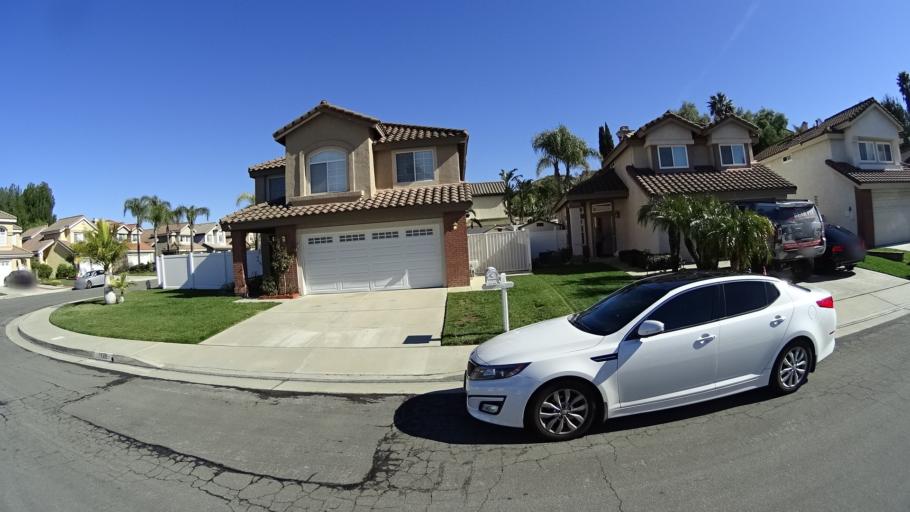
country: US
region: California
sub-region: Orange County
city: Villa Park
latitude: 33.8494
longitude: -117.7409
